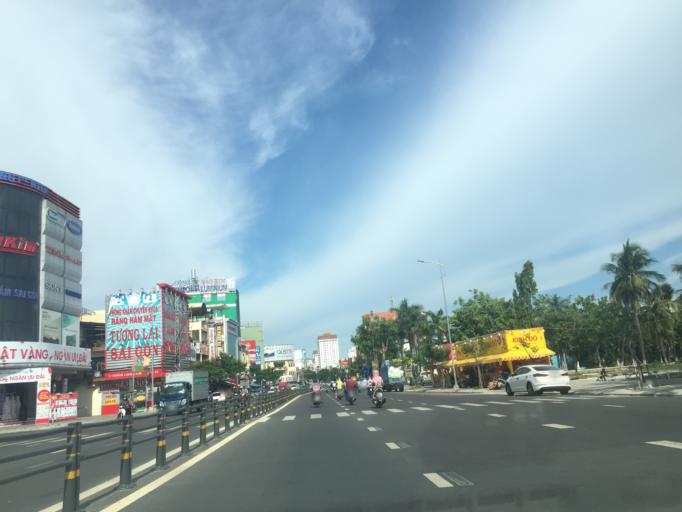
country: VN
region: Da Nang
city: Thanh Khe
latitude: 16.0659
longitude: 108.2047
